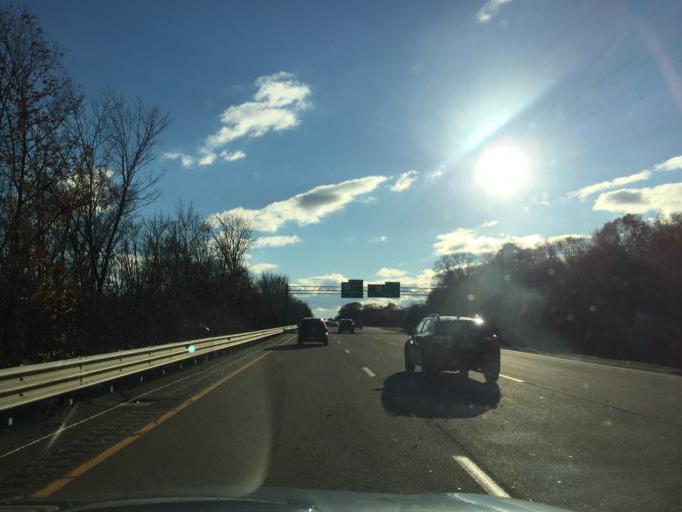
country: US
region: Massachusetts
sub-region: Bristol County
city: Attleboro
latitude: 41.9384
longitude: -71.3161
